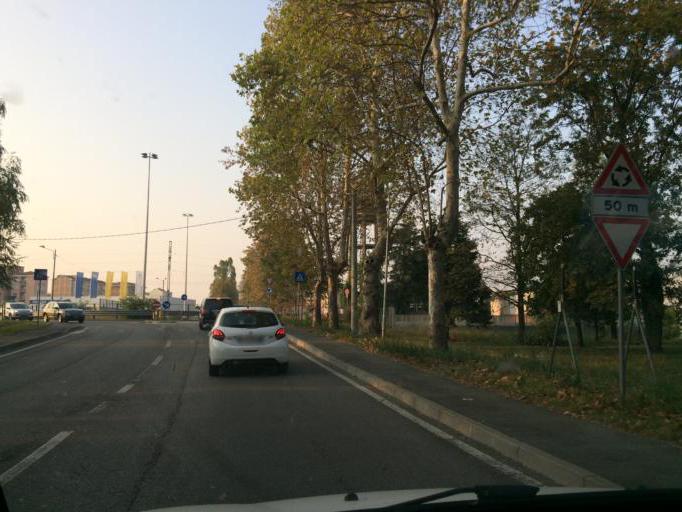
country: IT
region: Lombardy
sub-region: Provincia di Varese
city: Castellanza
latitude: 45.6117
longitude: 8.8877
